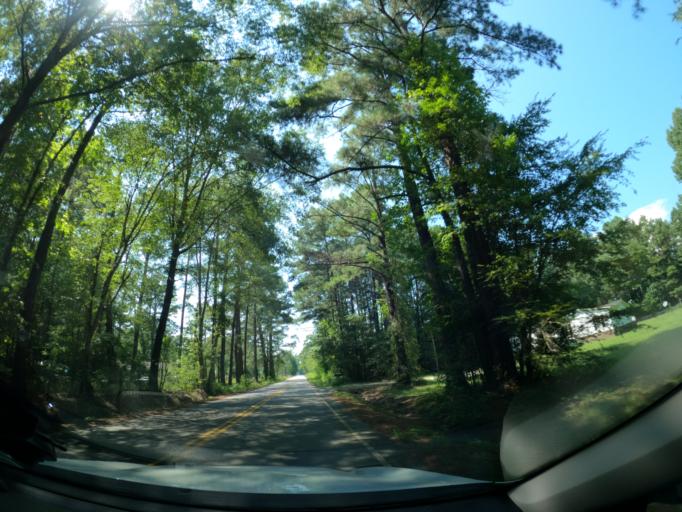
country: US
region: South Carolina
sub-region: Richland County
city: Hopkins
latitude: 33.8642
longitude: -80.8853
